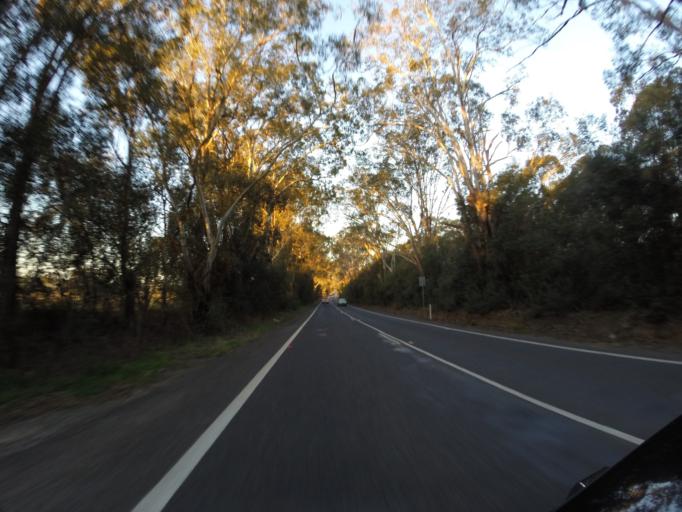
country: AU
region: New South Wales
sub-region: Camden
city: Cobbitty
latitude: -34.0153
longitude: 150.7066
